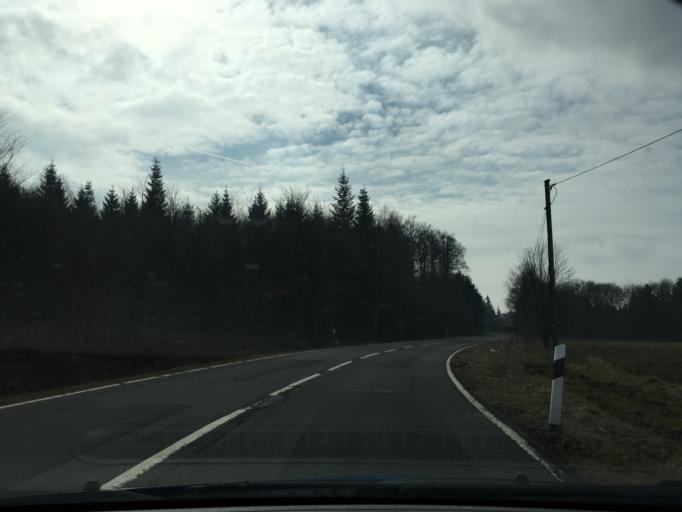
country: DE
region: Lower Saxony
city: Heinade
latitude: 51.7663
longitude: 9.5617
